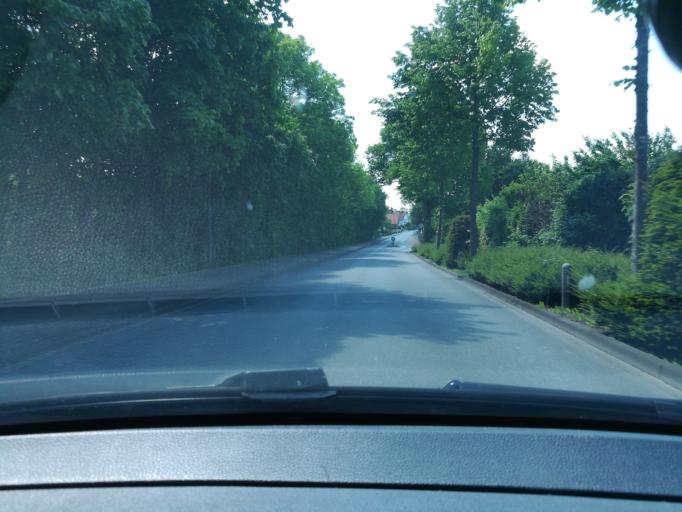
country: DE
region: North Rhine-Westphalia
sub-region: Regierungsbezirk Detmold
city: Herford
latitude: 52.1184
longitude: 8.7036
